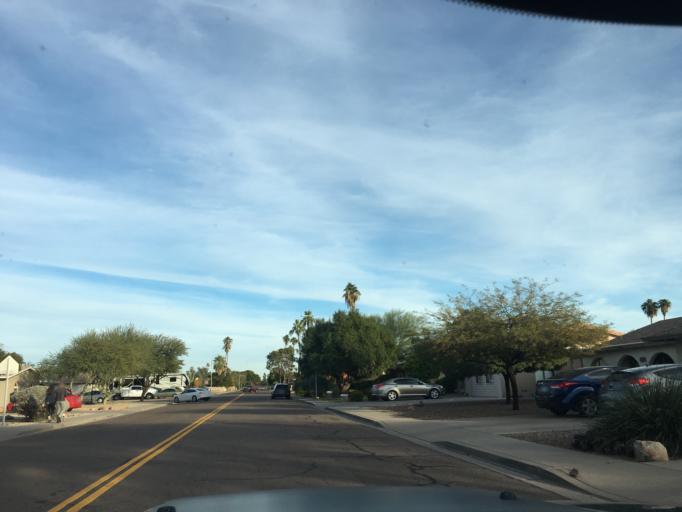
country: US
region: Arizona
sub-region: Maricopa County
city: Tempe
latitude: 33.3725
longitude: -111.9074
